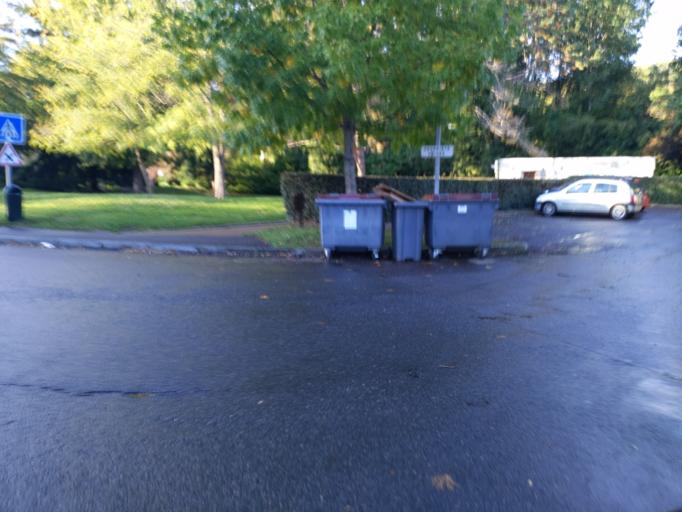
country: FR
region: Ile-de-France
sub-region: Departement des Yvelines
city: Saint-Remy-les-Chevreuse
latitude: 48.7019
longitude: 2.1011
